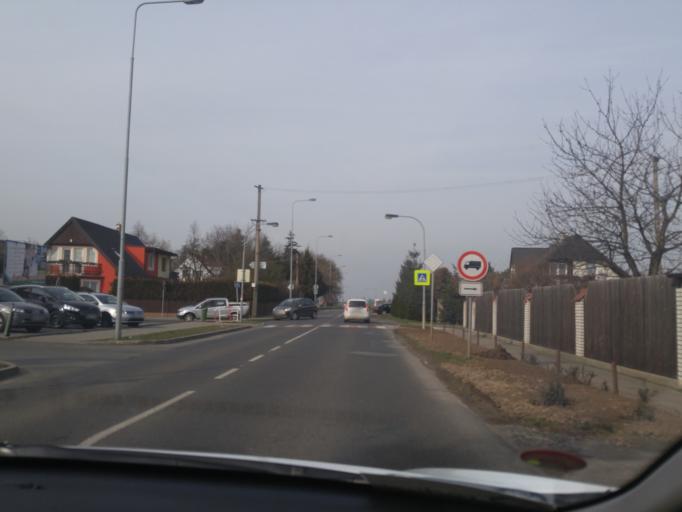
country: CZ
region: Central Bohemia
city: Brandys nad Labem-Stara Boleslav
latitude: 50.1899
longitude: 14.6502
